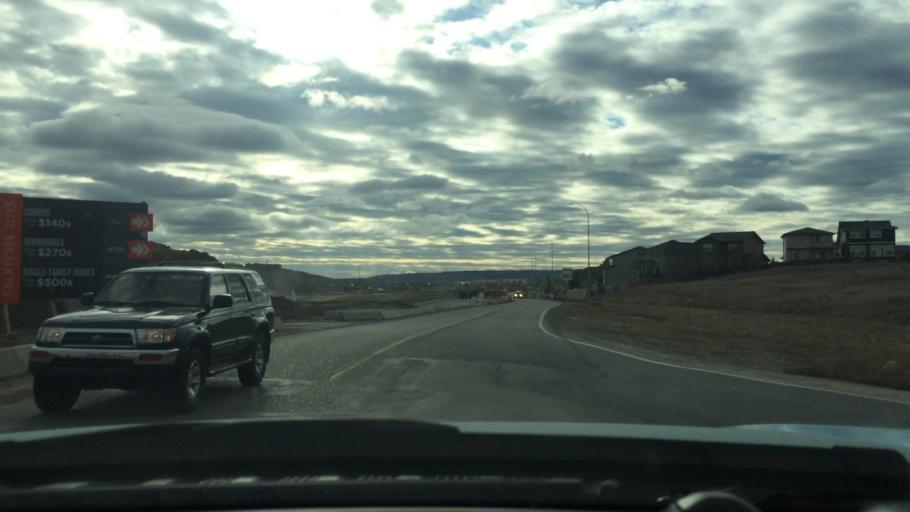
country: CA
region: Alberta
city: Calgary
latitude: 51.1832
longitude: -114.1351
